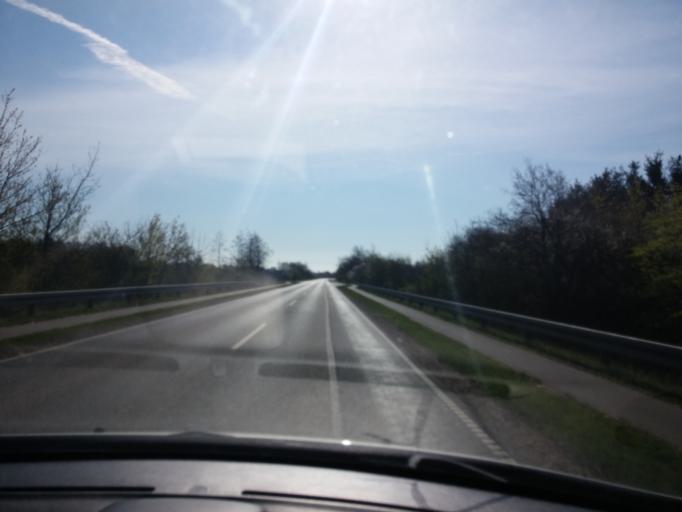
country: DK
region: Central Jutland
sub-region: Odder Kommune
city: Odder
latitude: 55.9610
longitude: 10.1786
